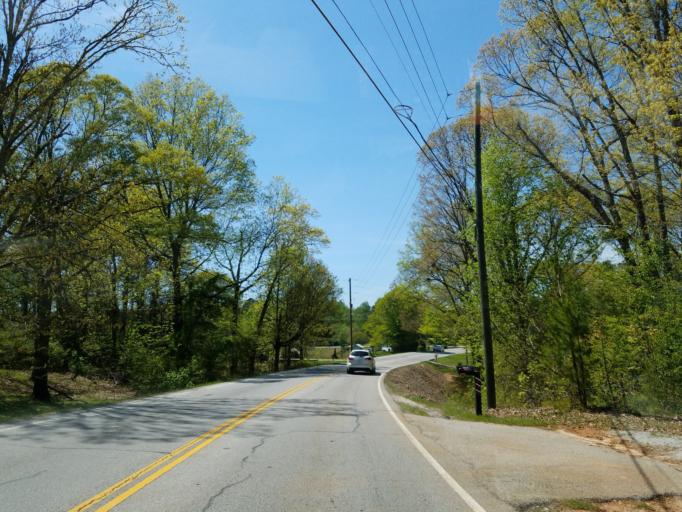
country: US
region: Georgia
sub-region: Paulding County
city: Hiram
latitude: 33.8654
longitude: -84.8009
